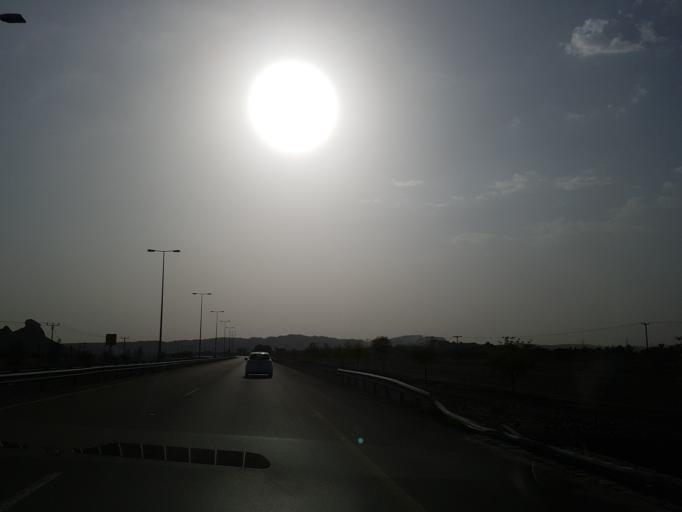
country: OM
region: Al Buraimi
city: Al Buraymi
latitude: 24.2439
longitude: 55.9851
